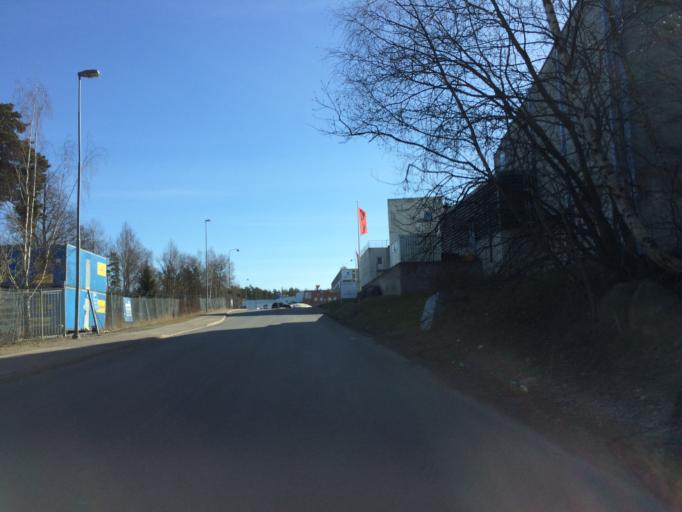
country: SE
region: Stockholm
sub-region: Huddinge Kommun
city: Segeltorp
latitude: 59.2628
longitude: 17.9029
